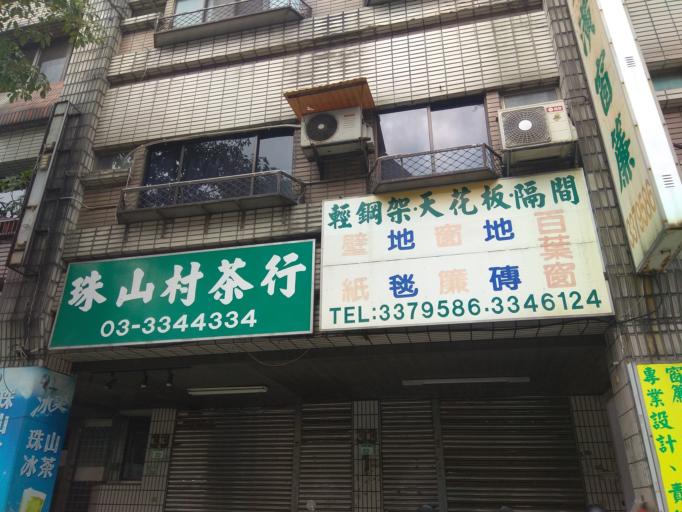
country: TW
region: Taiwan
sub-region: Taoyuan
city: Taoyuan
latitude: 24.9937
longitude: 121.3156
